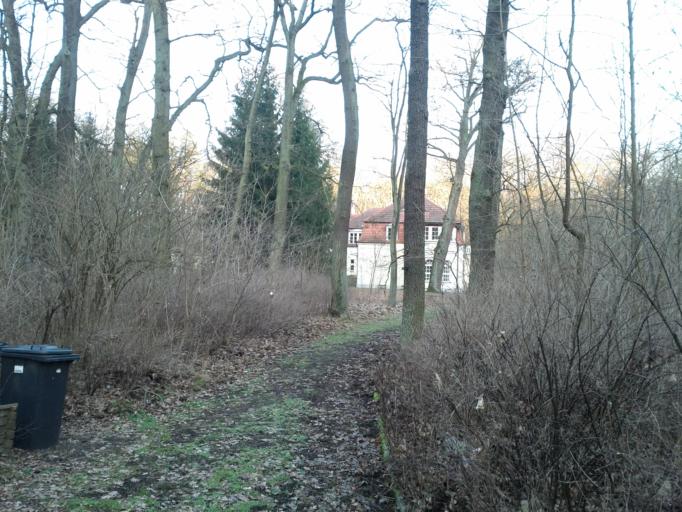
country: DE
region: Brandenburg
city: Grunheide
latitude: 52.4243
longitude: 13.7932
